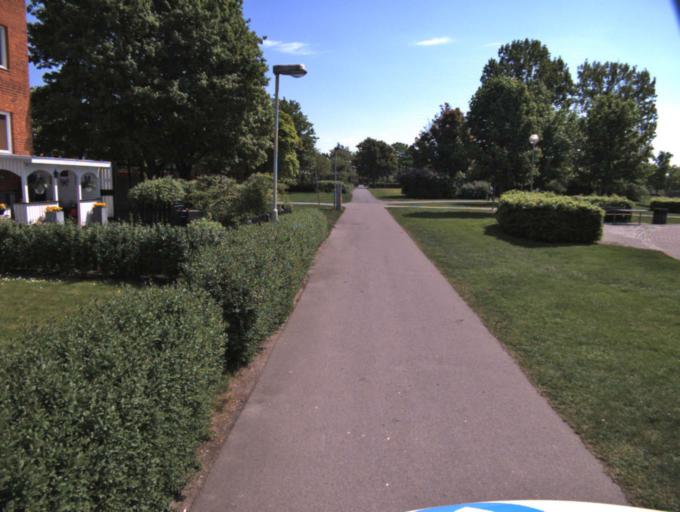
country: SE
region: Skane
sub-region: Kristianstads Kommun
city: Kristianstad
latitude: 56.0588
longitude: 14.1584
